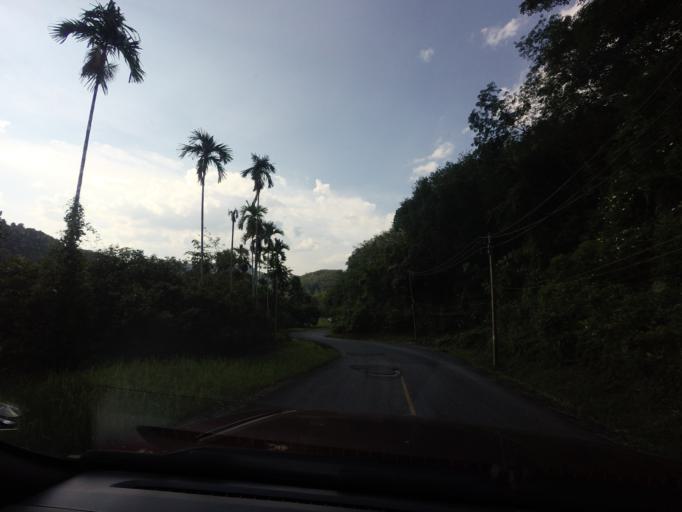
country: TH
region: Yala
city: Than To
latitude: 6.1502
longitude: 101.2810
